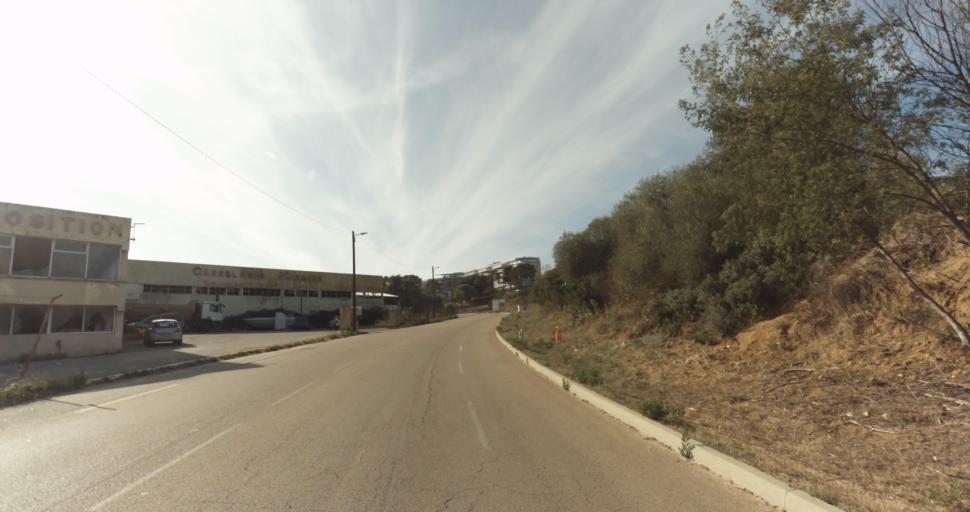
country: FR
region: Corsica
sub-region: Departement de la Corse-du-Sud
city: Ajaccio
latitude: 41.9294
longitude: 8.7666
